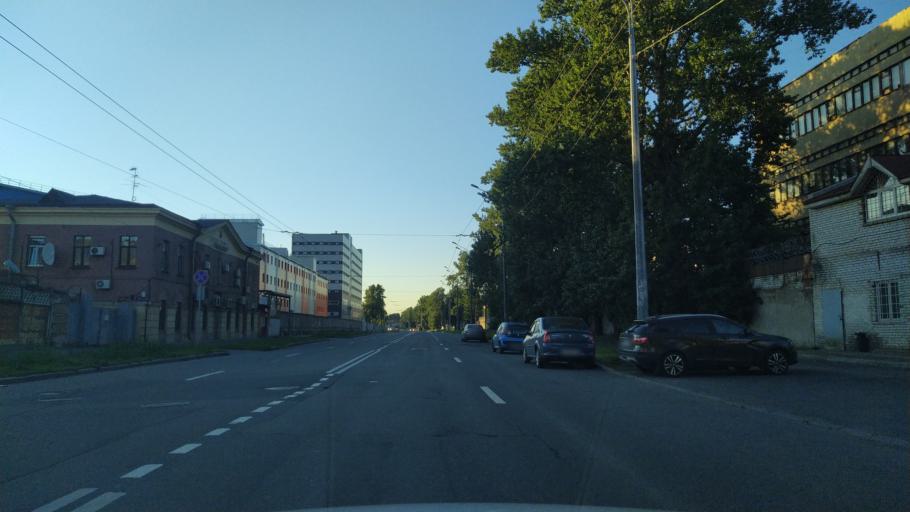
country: RU
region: Leningrad
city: Finlyandskiy
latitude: 59.9607
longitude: 30.3691
